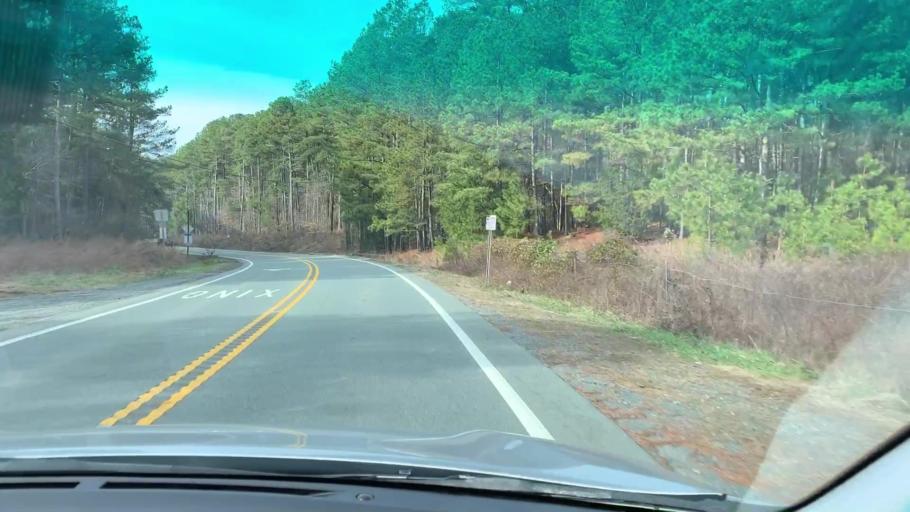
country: US
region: North Carolina
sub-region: Wake County
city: Green Level
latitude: 35.8470
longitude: -78.9261
